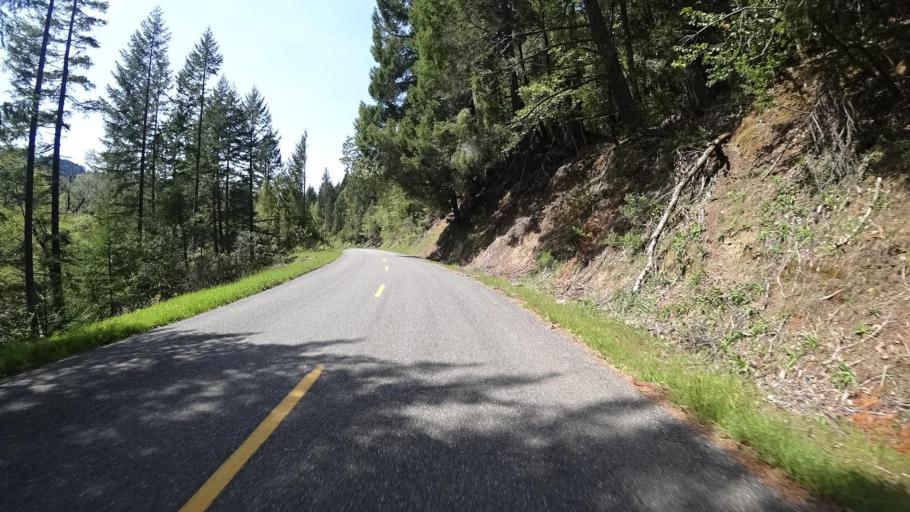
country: US
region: California
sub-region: Humboldt County
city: Redway
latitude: 40.3383
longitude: -123.6938
